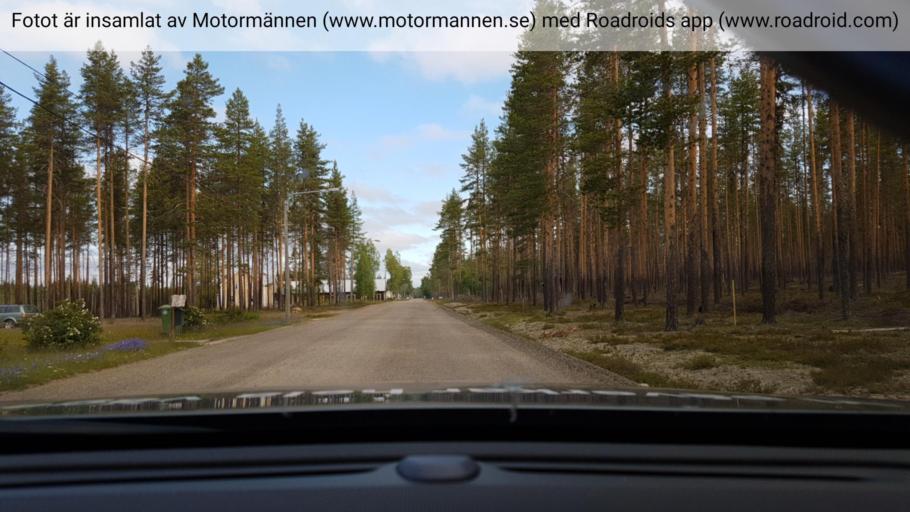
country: SE
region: Vaesterbotten
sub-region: Norsjo Kommun
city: Norsjoe
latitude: 64.6531
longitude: 19.2750
